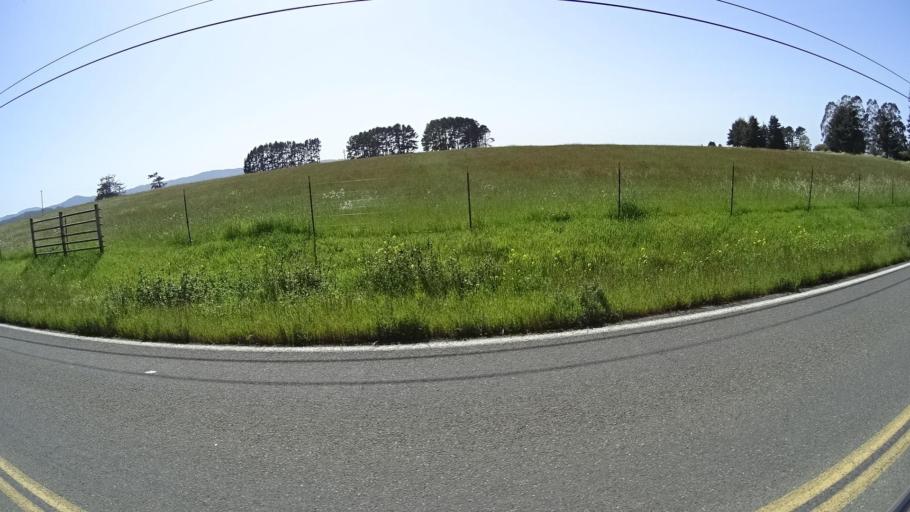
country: US
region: California
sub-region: Humboldt County
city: Hydesville
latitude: 40.5552
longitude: -124.1215
